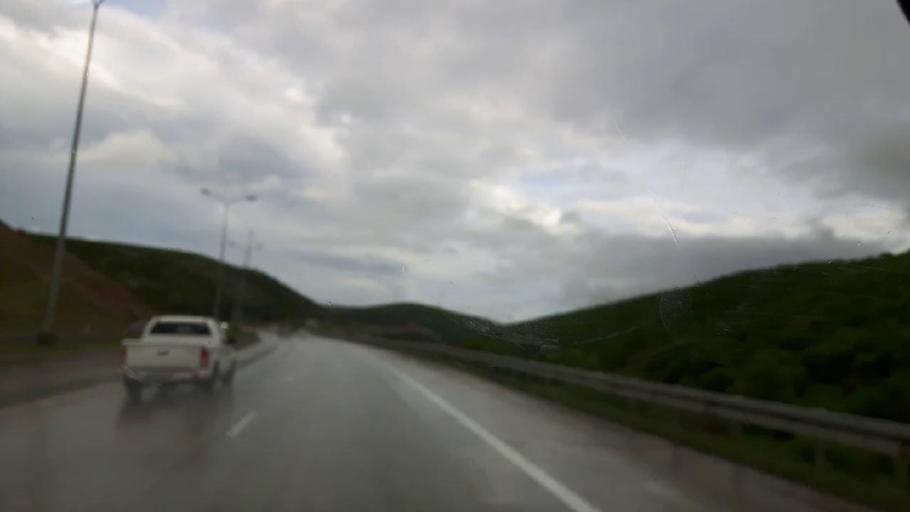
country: GE
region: Shida Kartli
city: Kaspi
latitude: 41.9969
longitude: 44.4008
